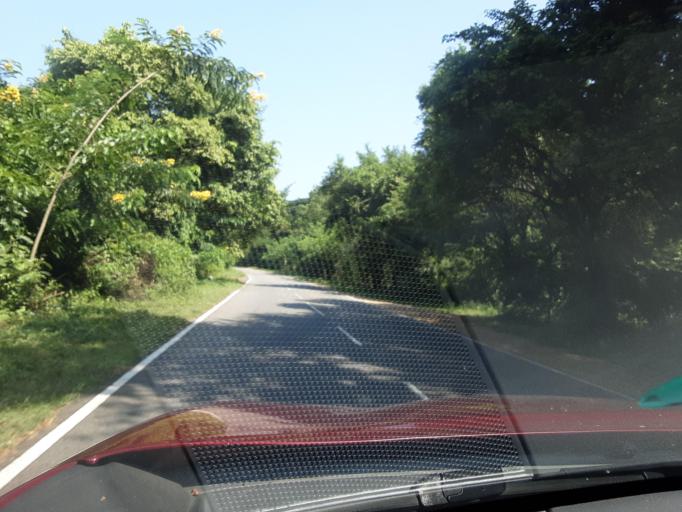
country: LK
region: Uva
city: Badulla
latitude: 7.2692
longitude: 81.0523
